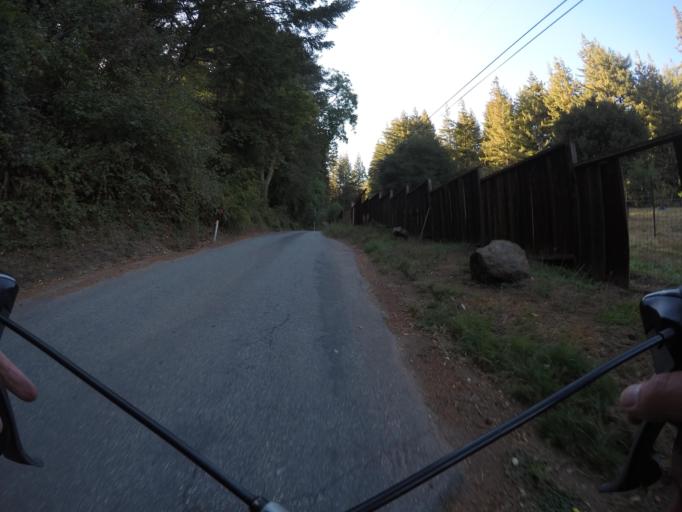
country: US
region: California
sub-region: Santa Cruz County
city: Ben Lomond
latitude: 37.1021
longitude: -122.0897
